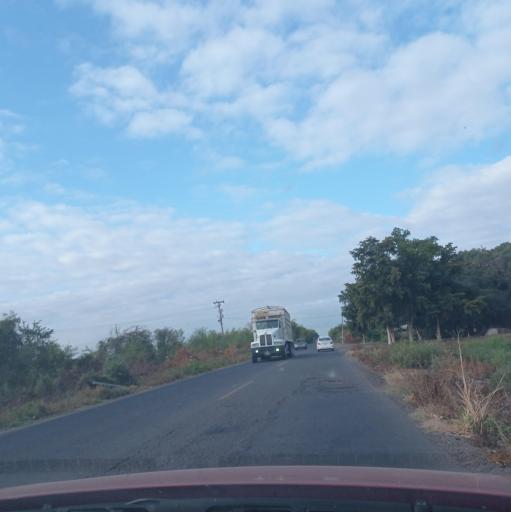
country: MX
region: Sinaloa
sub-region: Guasave
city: Las Quemazones
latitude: 25.6518
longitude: -108.5274
